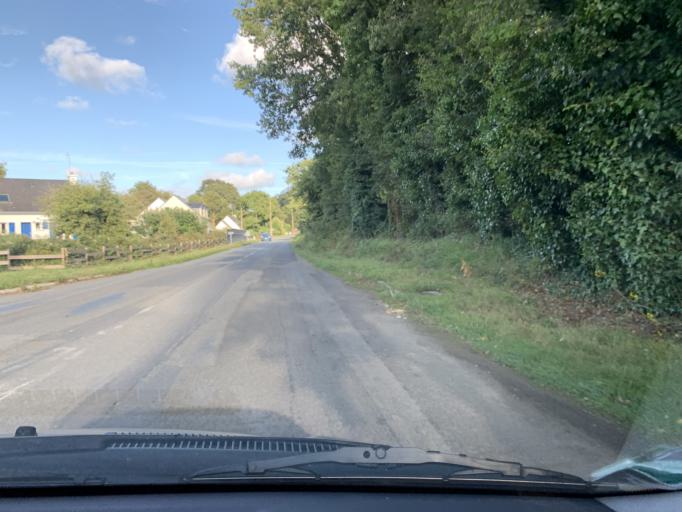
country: FR
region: Brittany
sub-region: Departement du Morbihan
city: Sarzeau
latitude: 47.5258
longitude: -2.7440
